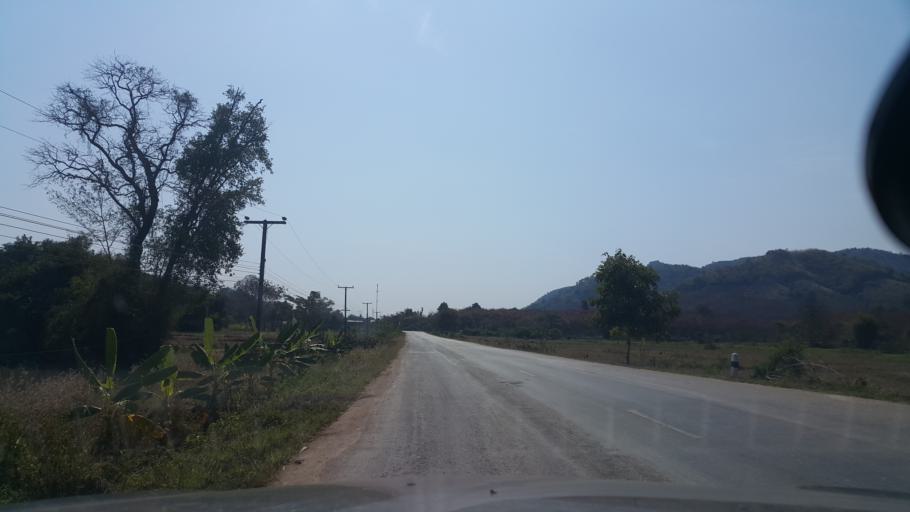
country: TH
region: Changwat Udon Thani
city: Na Yung
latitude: 17.8913
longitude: 102.0778
